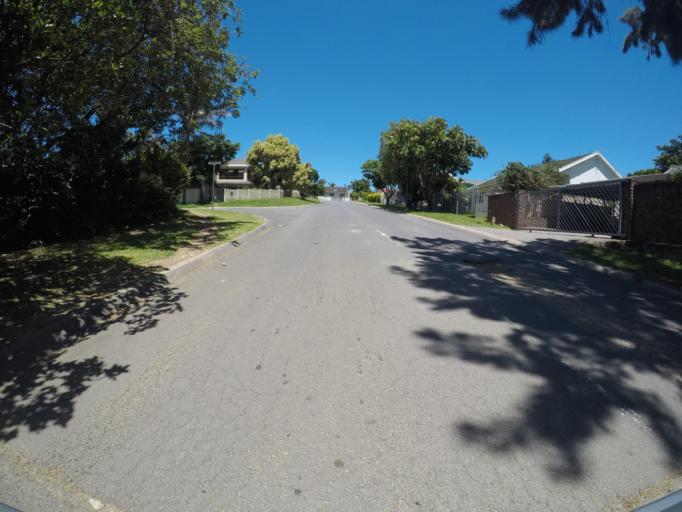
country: ZA
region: Eastern Cape
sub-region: Buffalo City Metropolitan Municipality
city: East London
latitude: -32.9561
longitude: 27.9372
